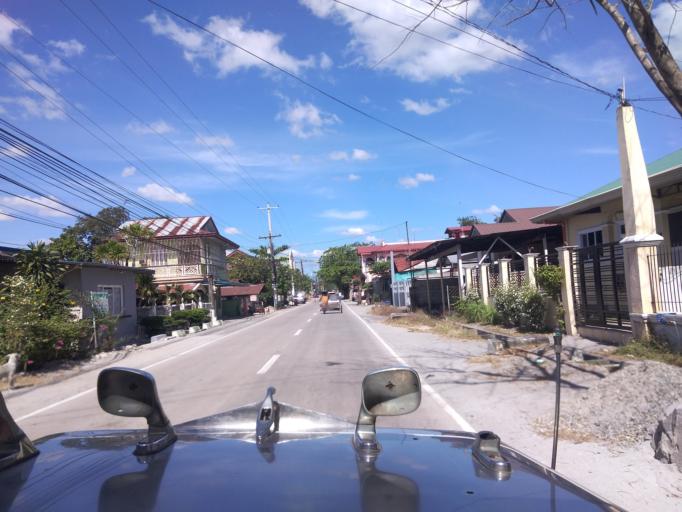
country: PH
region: Central Luzon
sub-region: Province of Pampanga
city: Santa Rita
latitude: 15.0011
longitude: 120.6100
